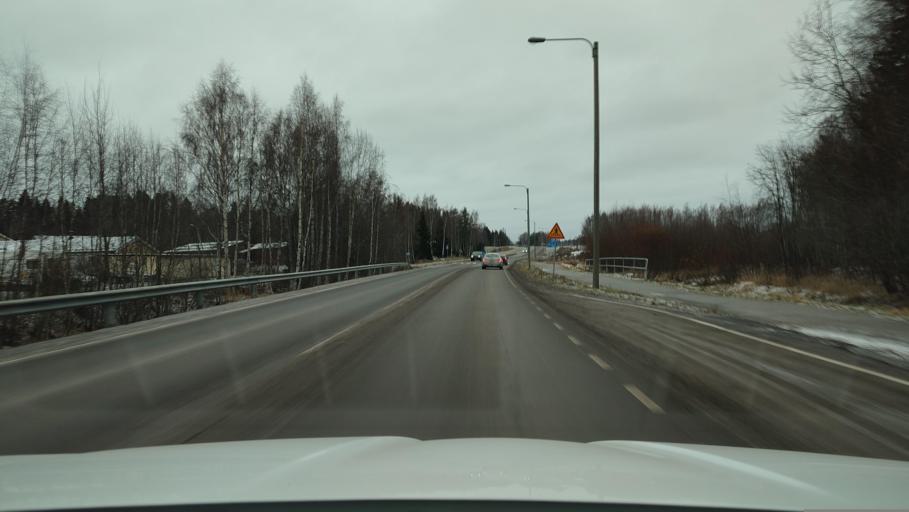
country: FI
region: Ostrobothnia
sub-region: Vaasa
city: Smedsby
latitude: 63.1226
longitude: 21.7064
